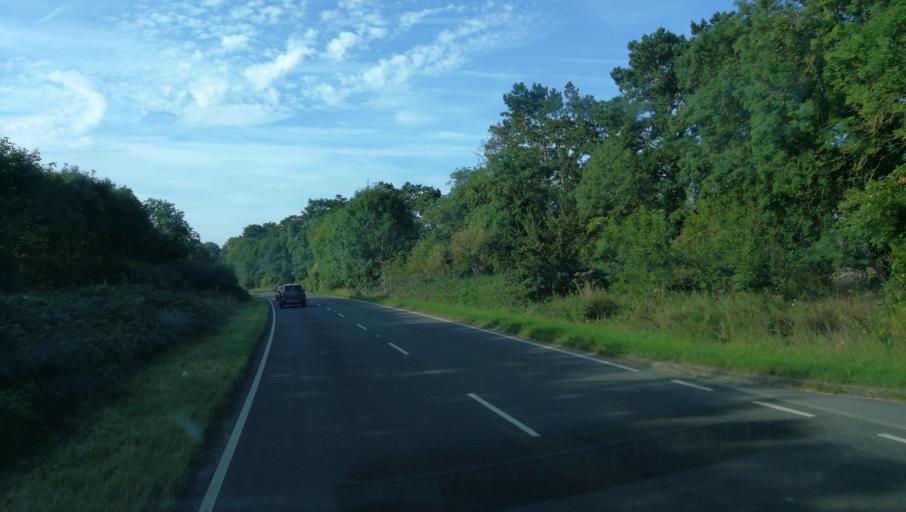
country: GB
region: England
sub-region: Oxfordshire
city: Somerton
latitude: 51.9118
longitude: -1.3284
